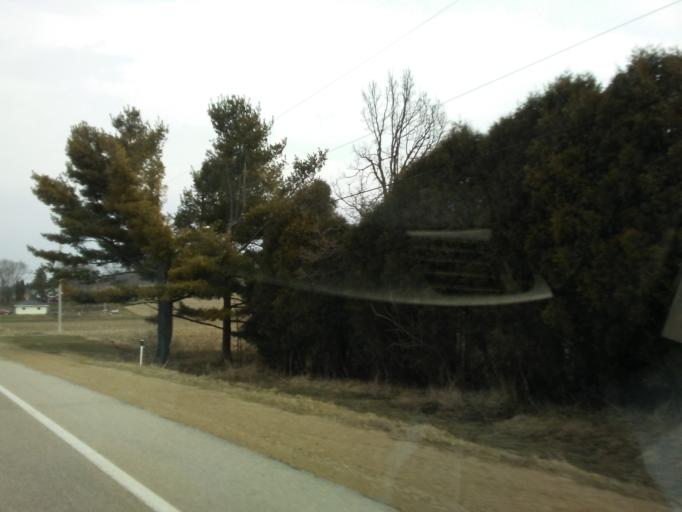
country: US
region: Wisconsin
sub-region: Columbia County
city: Lodi
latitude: 43.2991
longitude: -89.5236
